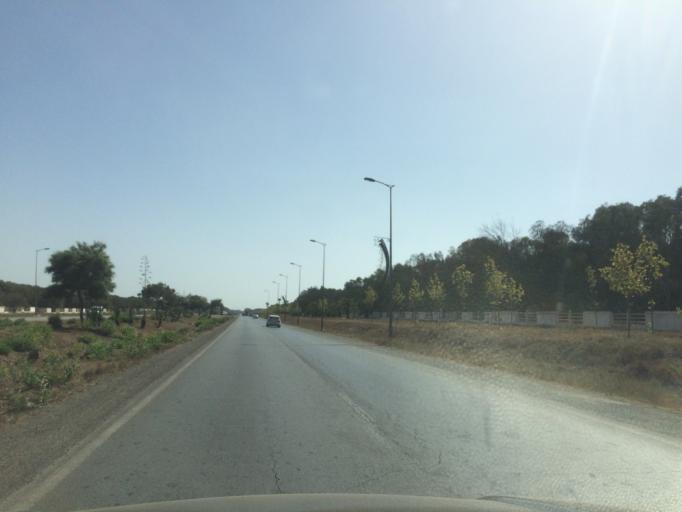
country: MA
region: Rabat-Sale-Zemmour-Zaer
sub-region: Skhirate-Temara
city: Temara
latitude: 33.9607
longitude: -6.9069
